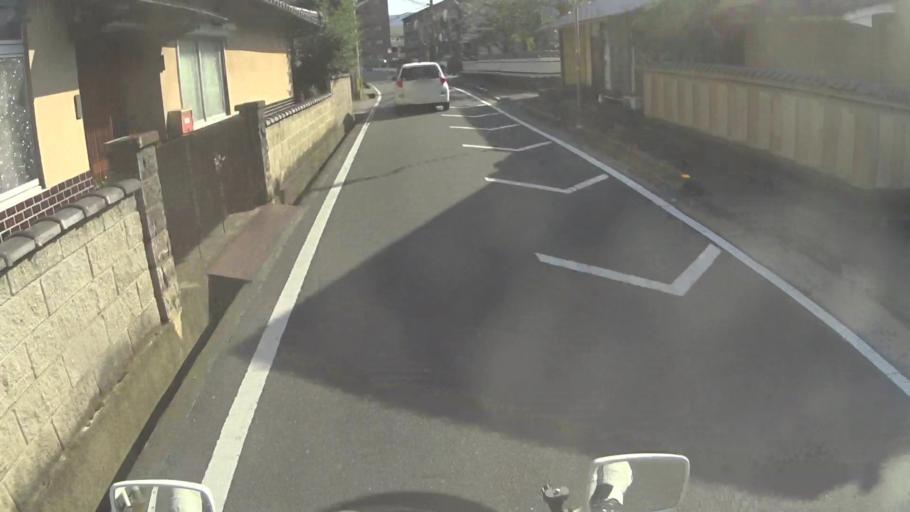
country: JP
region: Kyoto
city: Kameoka
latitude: 35.0090
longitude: 135.6017
